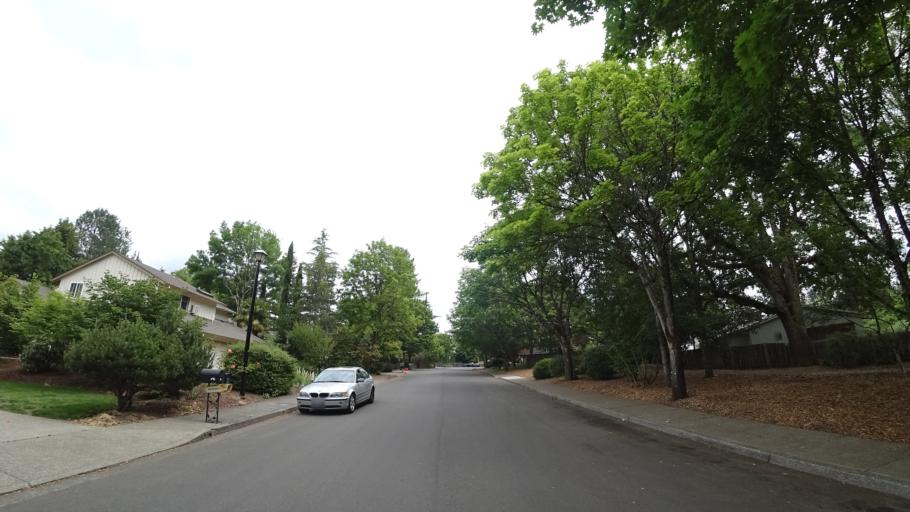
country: US
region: Oregon
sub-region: Washington County
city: Garden Home-Whitford
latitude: 45.4624
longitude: -122.7596
